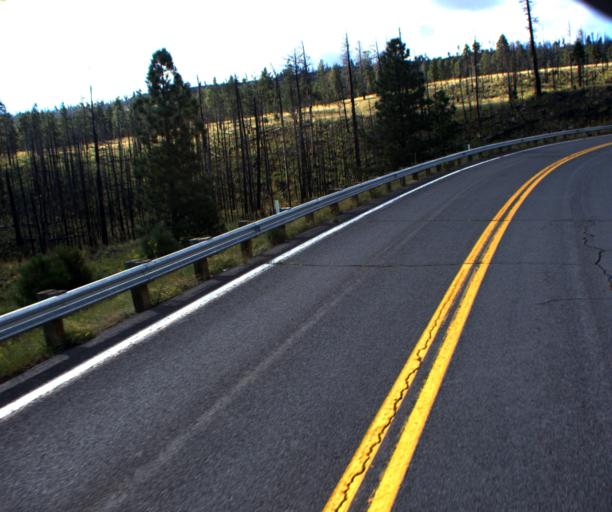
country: US
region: Arizona
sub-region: Apache County
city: Eagar
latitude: 34.0517
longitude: -109.3476
